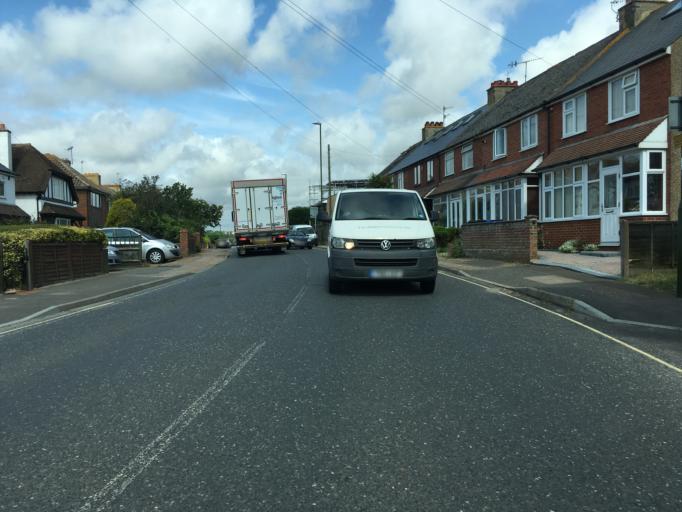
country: GB
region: England
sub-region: West Sussex
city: Shoreham-by-Sea
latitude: 50.8360
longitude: -0.2813
